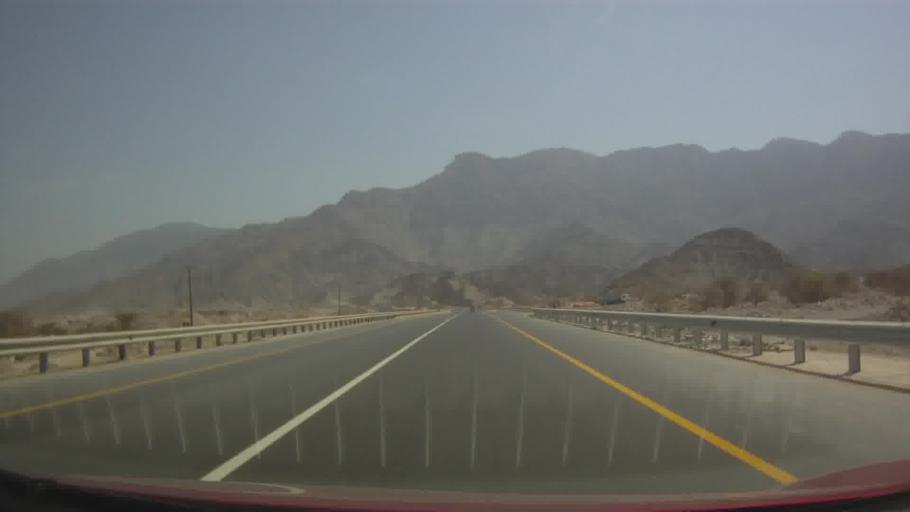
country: OM
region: Muhafazat Masqat
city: Muscat
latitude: 23.4064
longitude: 58.7801
